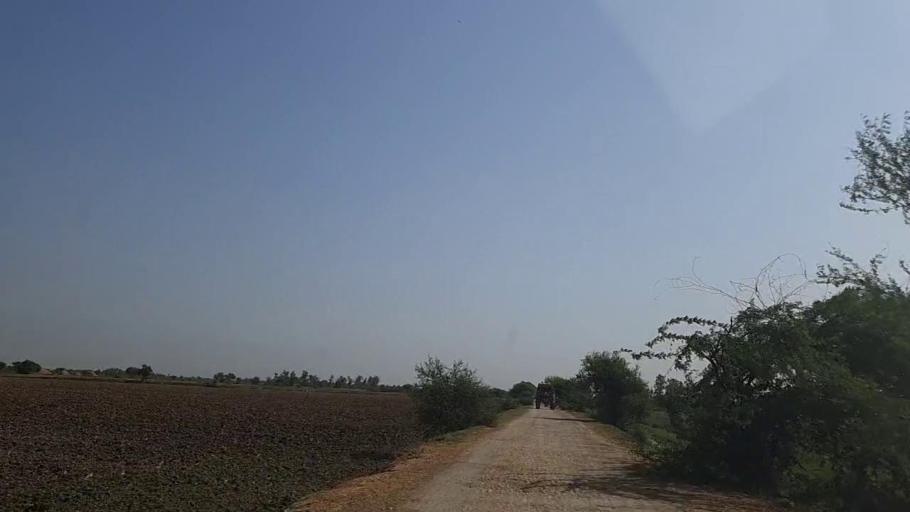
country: PK
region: Sindh
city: Daro Mehar
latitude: 24.7209
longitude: 68.1026
